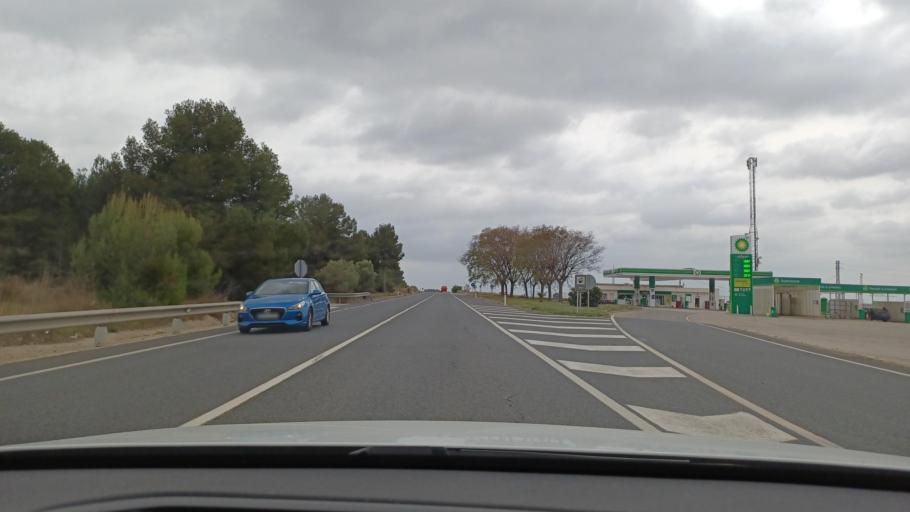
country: ES
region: Catalonia
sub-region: Provincia de Tarragona
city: la Pobla de Mafumet
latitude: 41.1749
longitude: 1.2401
